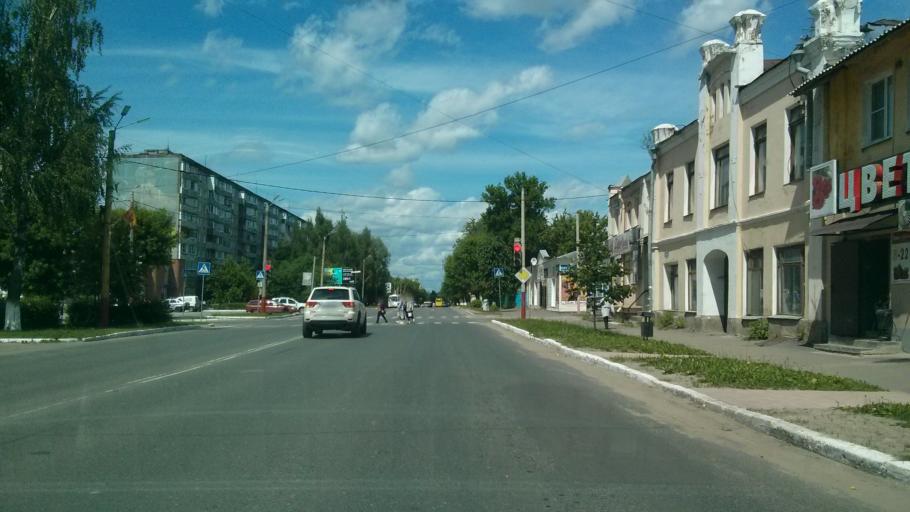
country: RU
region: Vladimir
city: Murom
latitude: 55.5725
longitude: 42.0573
